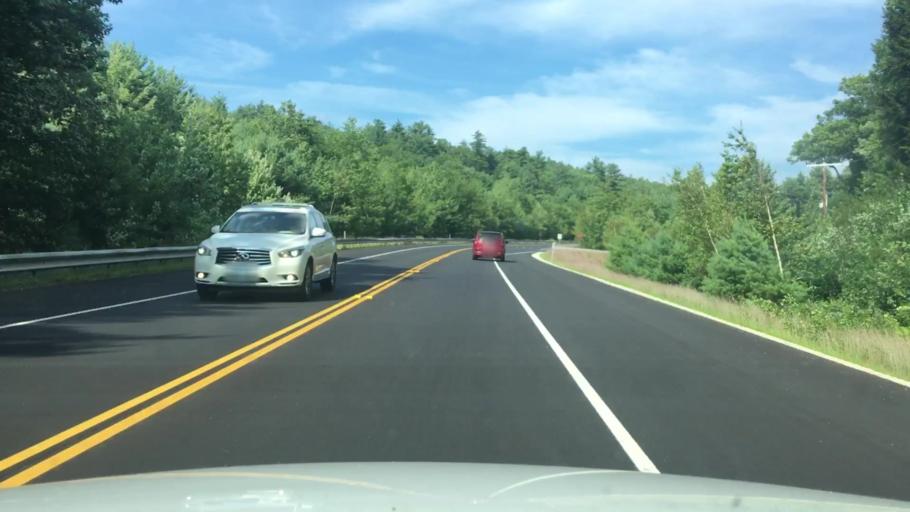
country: US
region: New Hampshire
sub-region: Belknap County
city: Gilford
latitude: 43.5377
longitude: -71.4321
